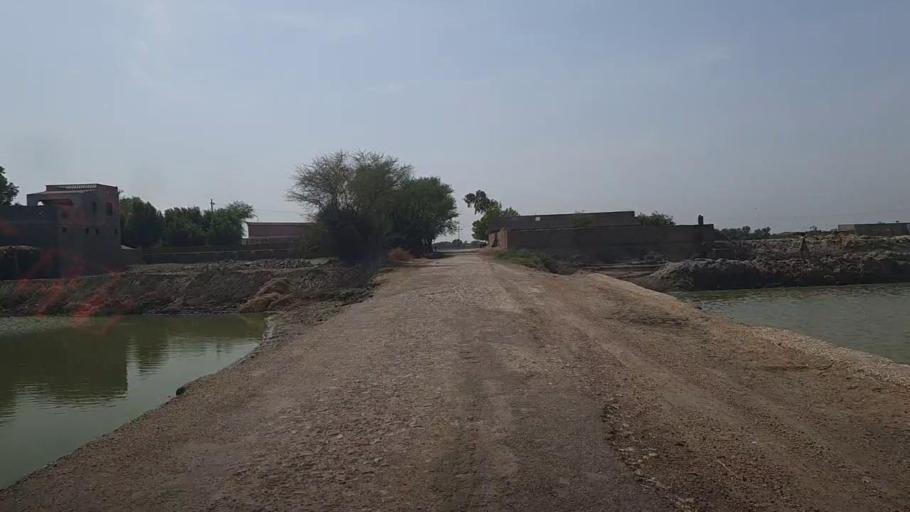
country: PK
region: Sindh
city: Ubauro
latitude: 28.1368
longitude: 69.8253
